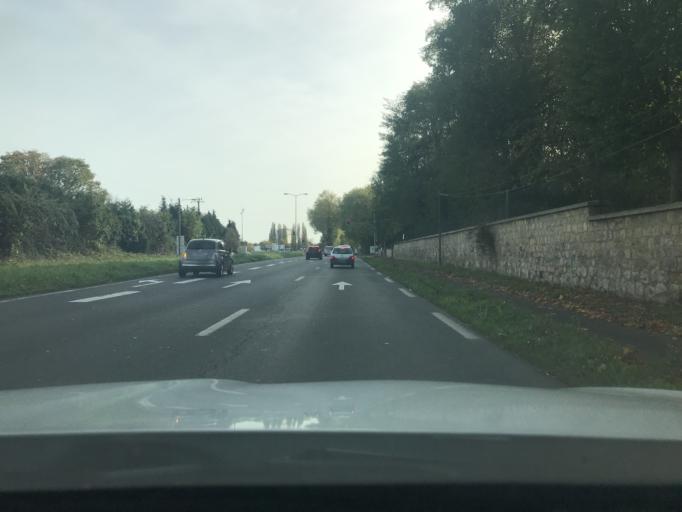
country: FR
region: Lower Normandy
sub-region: Departement du Calvados
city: Epron
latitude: 49.2237
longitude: -0.3688
